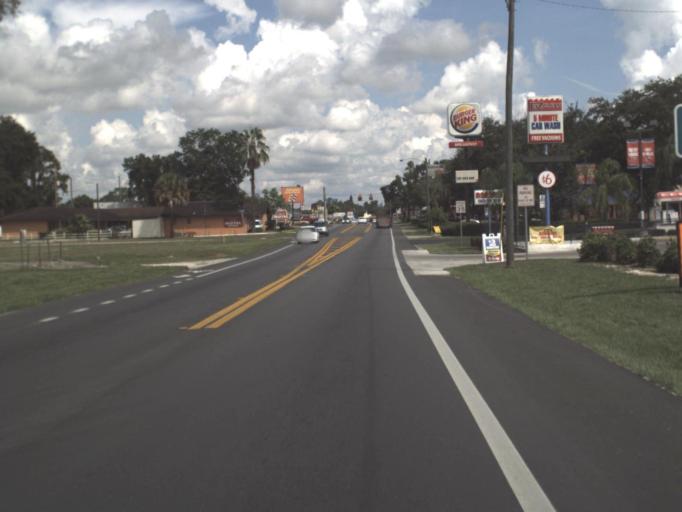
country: US
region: Florida
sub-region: Pasco County
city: Zephyrhills
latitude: 28.2380
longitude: -82.1840
